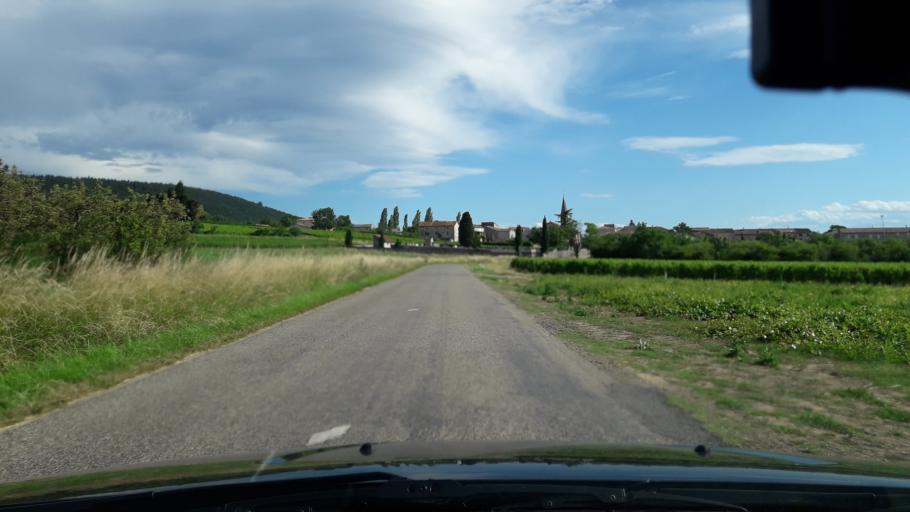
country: FR
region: Rhone-Alpes
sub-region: Departement de l'Ardeche
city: Lavilledieu
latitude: 44.6151
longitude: 4.4744
